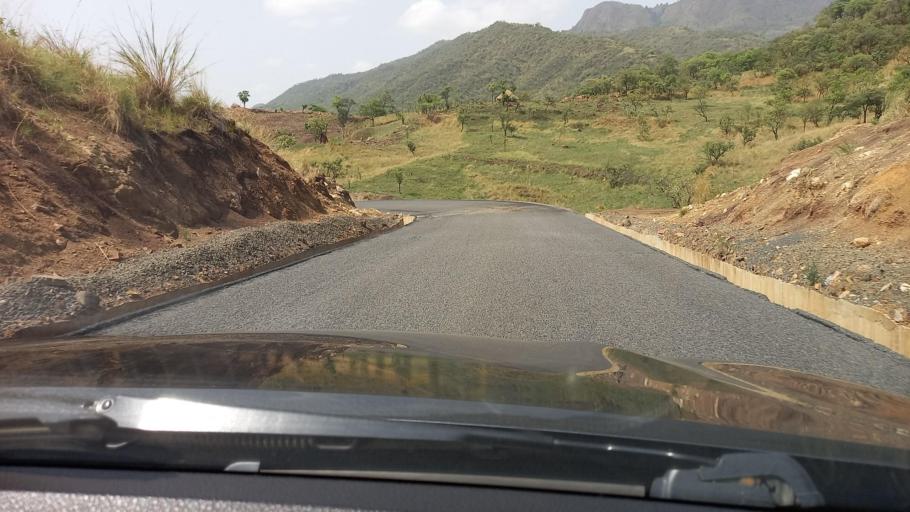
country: ET
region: Southern Nations, Nationalities, and People's Region
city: Mizan Teferi
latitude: 6.1948
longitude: 35.6730
